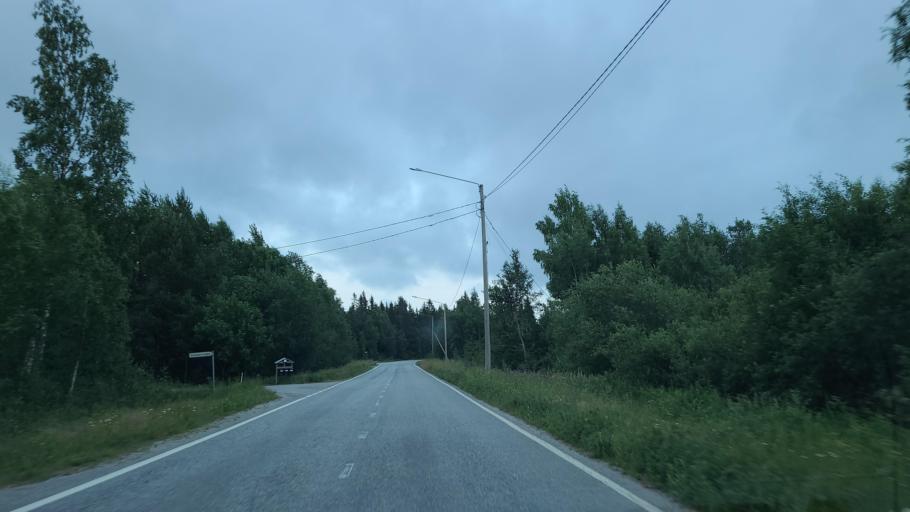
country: FI
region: Ostrobothnia
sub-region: Vaasa
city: Replot
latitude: 63.2807
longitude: 21.1306
